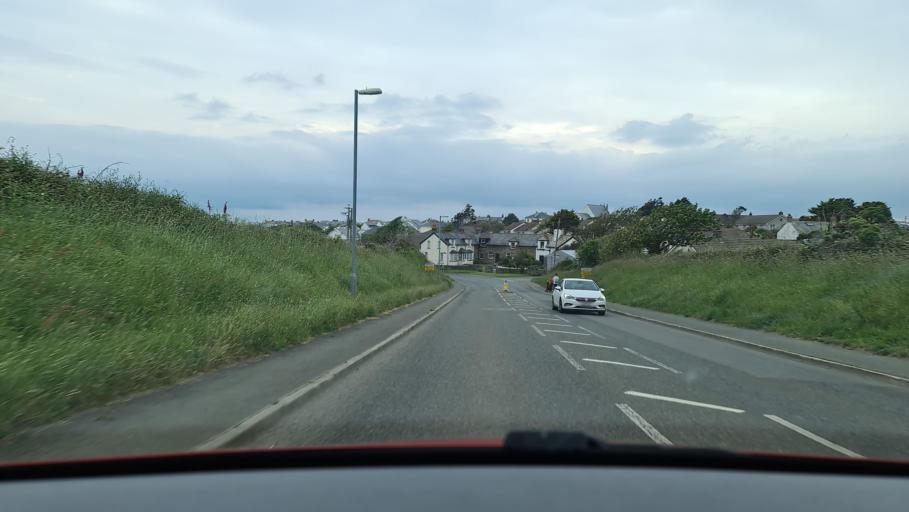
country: GB
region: England
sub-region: Cornwall
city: Tintagel
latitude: 50.6593
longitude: -4.7492
